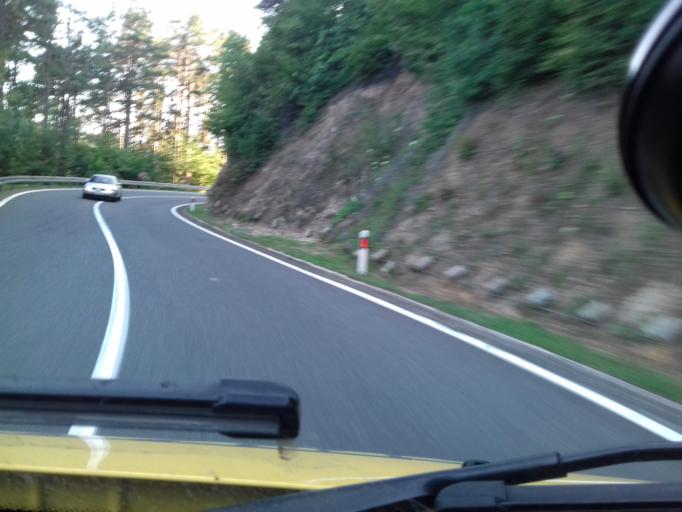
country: BA
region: Federation of Bosnia and Herzegovina
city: Ostrozac
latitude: 44.9031
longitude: 15.9385
